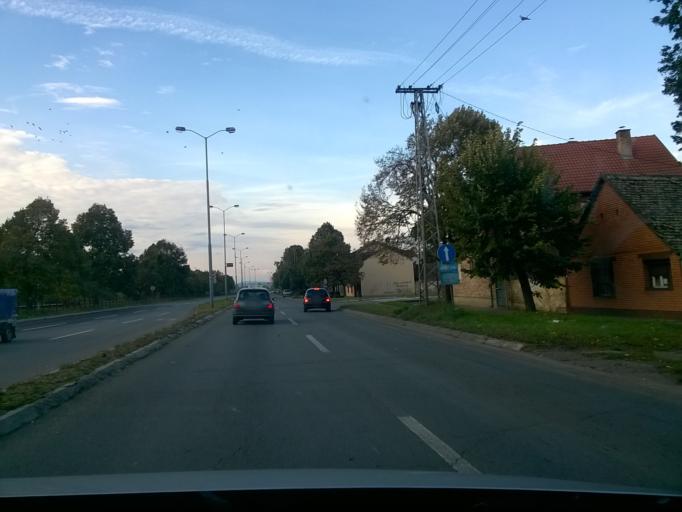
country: RS
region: Autonomna Pokrajina Vojvodina
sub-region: Juznobanatski Okrug
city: Pancevo
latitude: 44.8604
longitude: 20.6561
